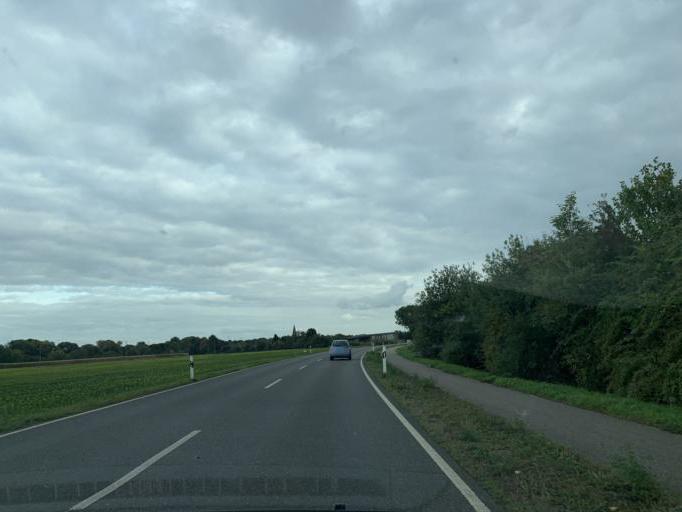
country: DE
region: North Rhine-Westphalia
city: Huckelhoven
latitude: 51.0430
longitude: 6.2061
